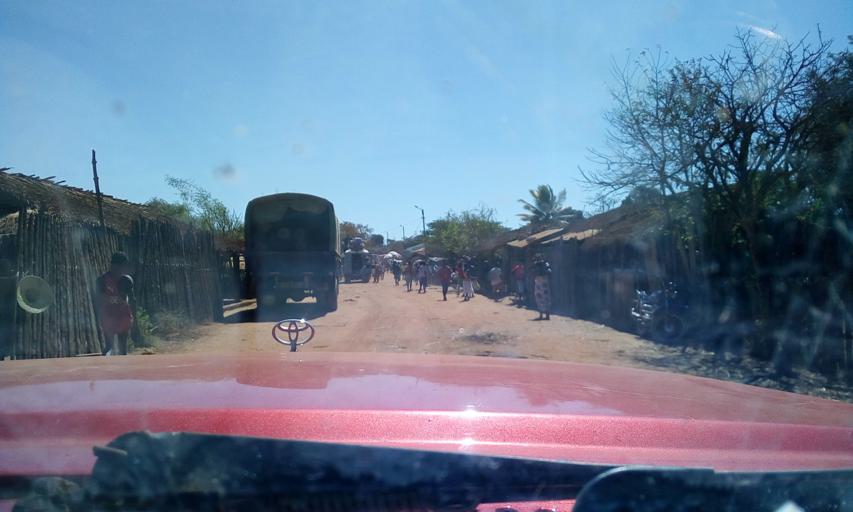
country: MG
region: Boeny
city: Mahajanga
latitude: -15.9581
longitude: 45.9397
